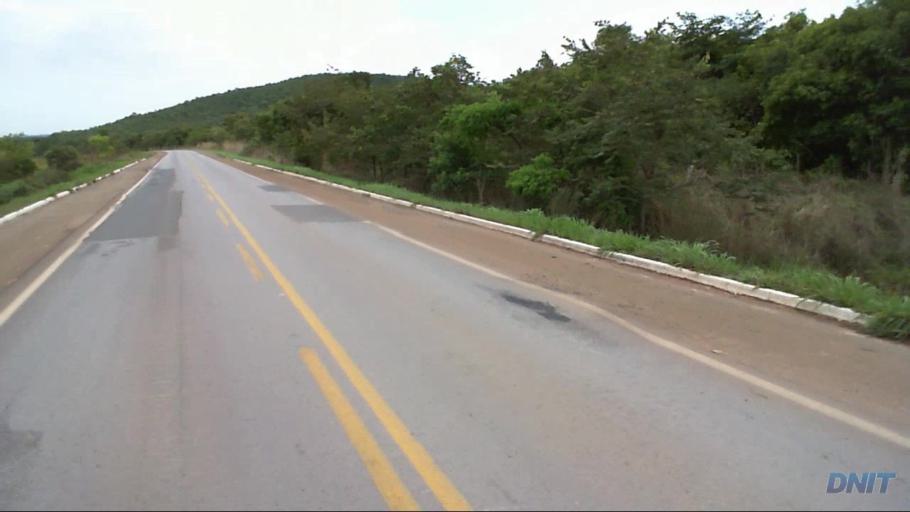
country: BR
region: Goias
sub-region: Barro Alto
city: Barro Alto
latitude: -14.9000
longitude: -48.9651
